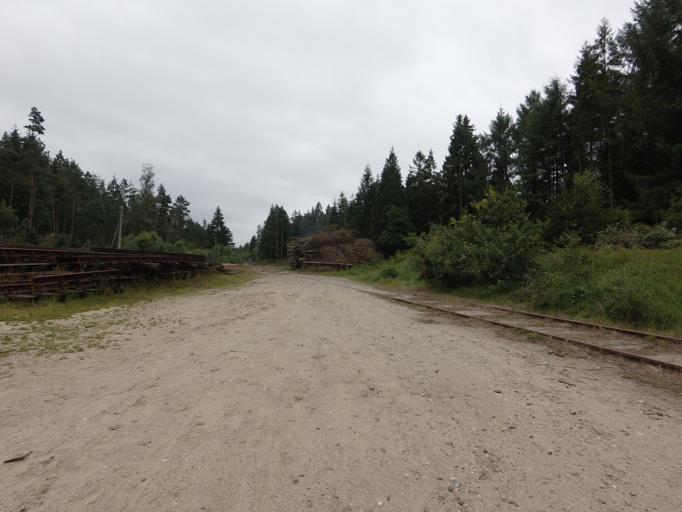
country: DK
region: Central Jutland
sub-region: Silkeborg Kommune
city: Virklund
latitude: 56.0395
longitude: 9.4704
